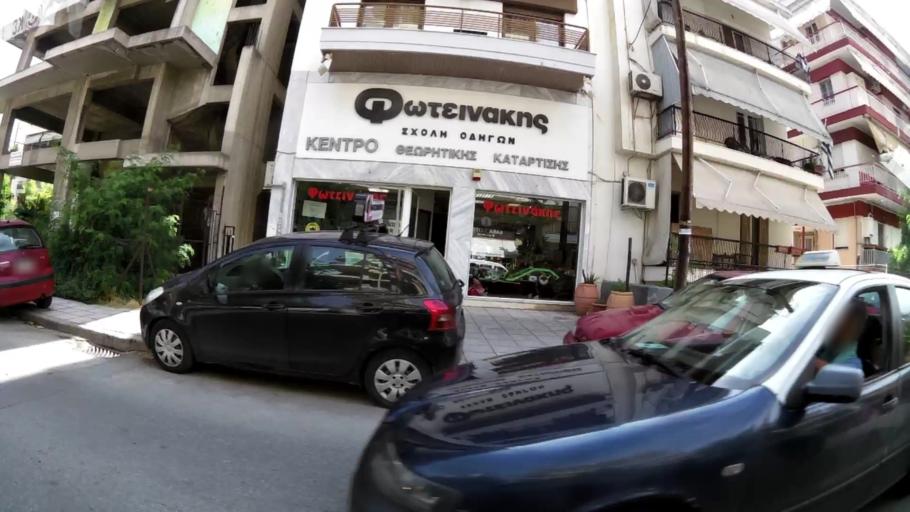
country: GR
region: Central Macedonia
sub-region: Nomos Thessalonikis
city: Triandria
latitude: 40.6083
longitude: 22.9700
